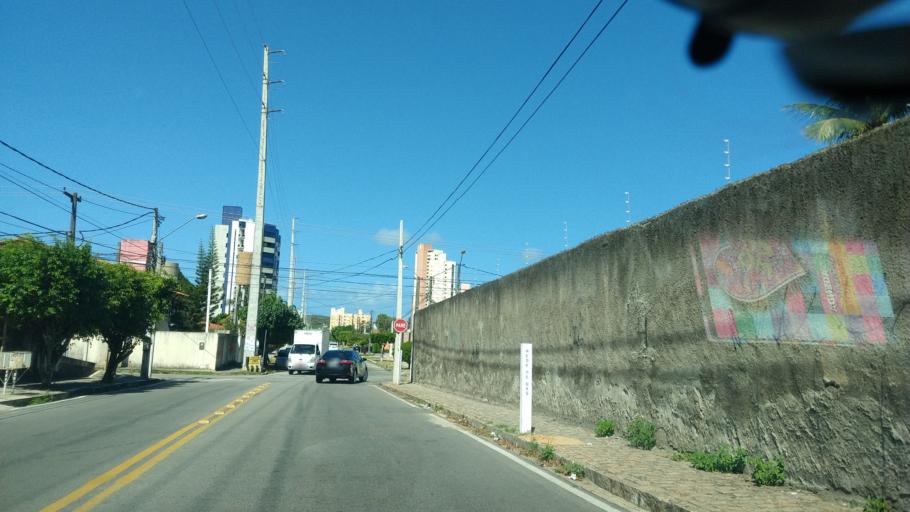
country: BR
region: Rio Grande do Norte
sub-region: Natal
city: Natal
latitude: -5.8677
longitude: -35.1969
